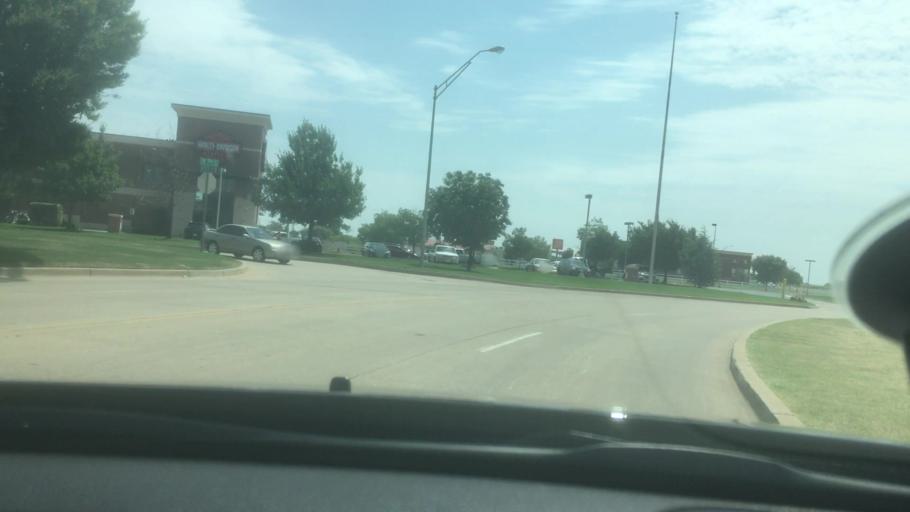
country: US
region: Oklahoma
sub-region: Oklahoma County
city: Bethany
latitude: 35.4628
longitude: -97.6352
